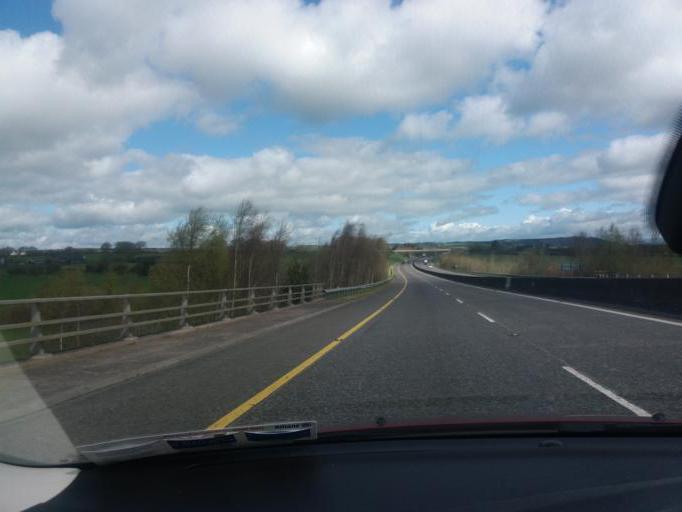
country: IE
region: Munster
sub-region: County Cork
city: Rathcormac
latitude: 52.0613
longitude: -8.3047
